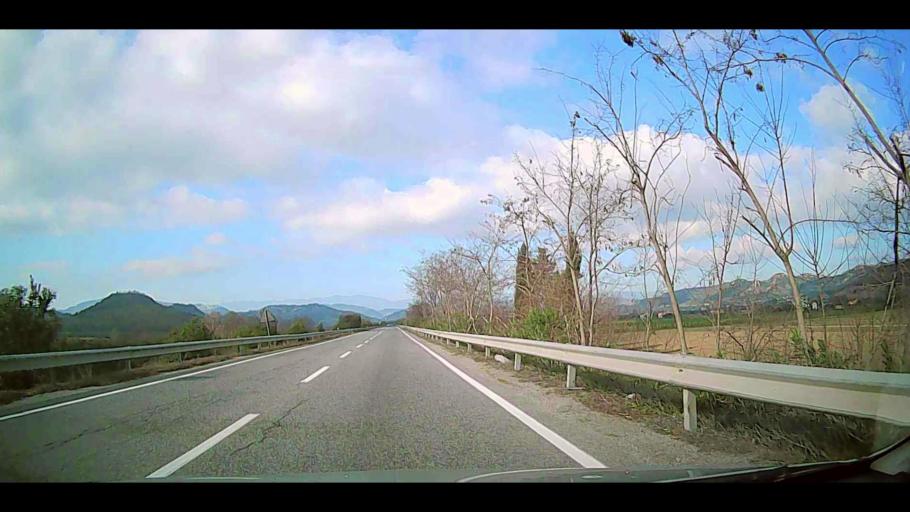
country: IT
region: Calabria
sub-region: Provincia di Crotone
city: Rocca di Neto
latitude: 39.1693
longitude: 16.9768
